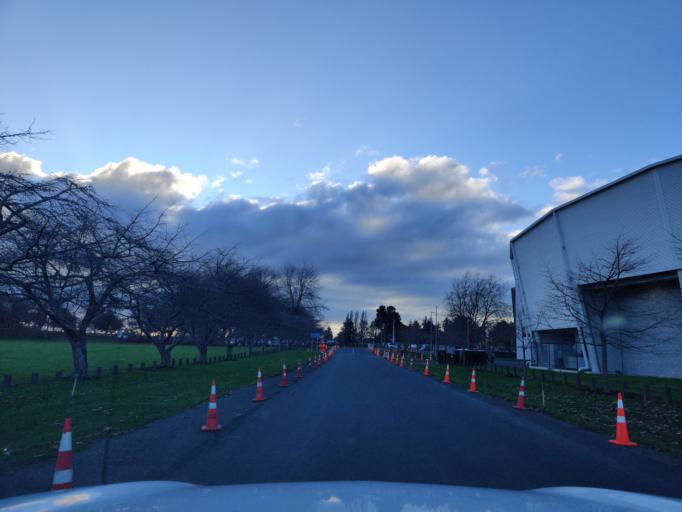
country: NZ
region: Waikato
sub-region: Waipa District
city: Cambridge
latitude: -37.8905
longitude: 175.4345
